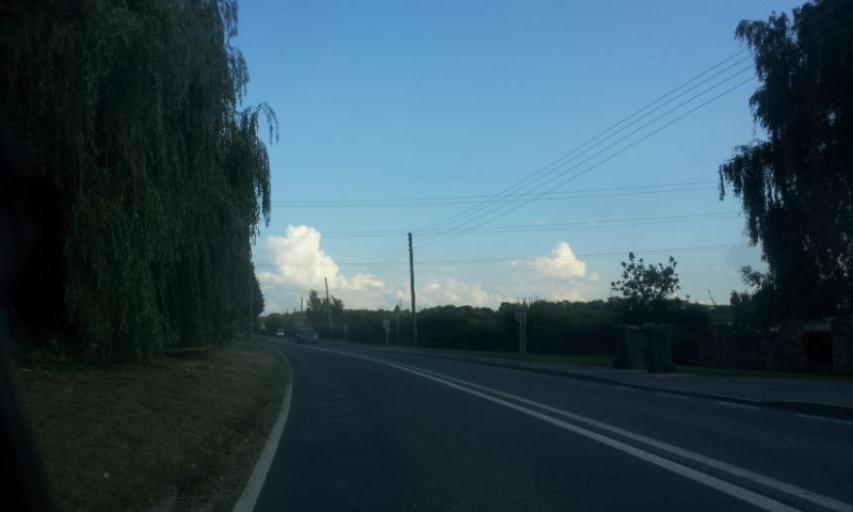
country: GB
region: England
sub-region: Kent
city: Longfield
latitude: 51.4053
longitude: 0.2829
